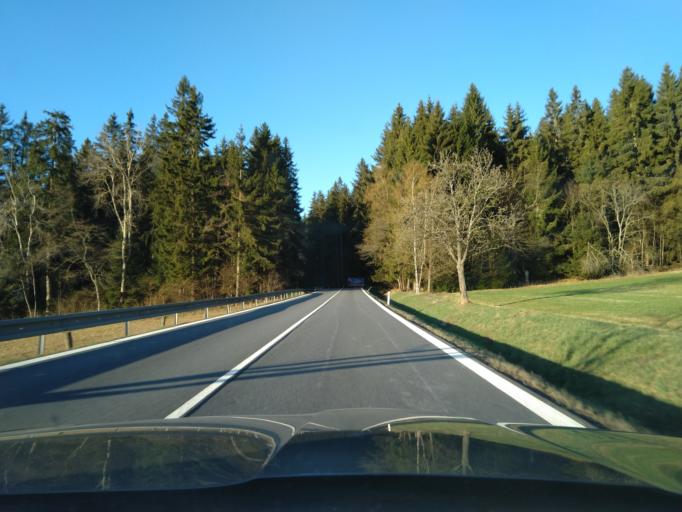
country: CZ
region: Jihocesky
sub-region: Okres Prachatice
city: Vimperk
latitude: 49.0087
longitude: 13.7672
